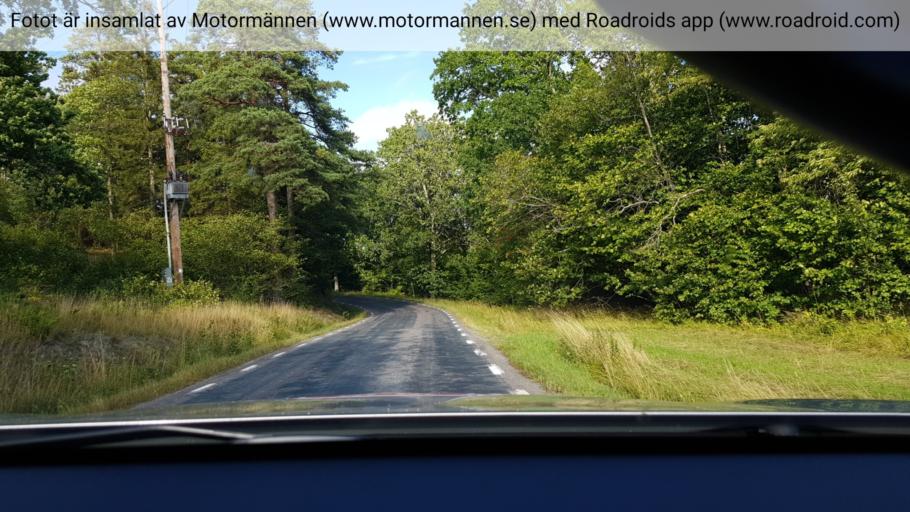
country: SE
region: Stockholm
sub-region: Nynashamns Kommun
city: Osmo
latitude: 58.8948
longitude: 17.7938
